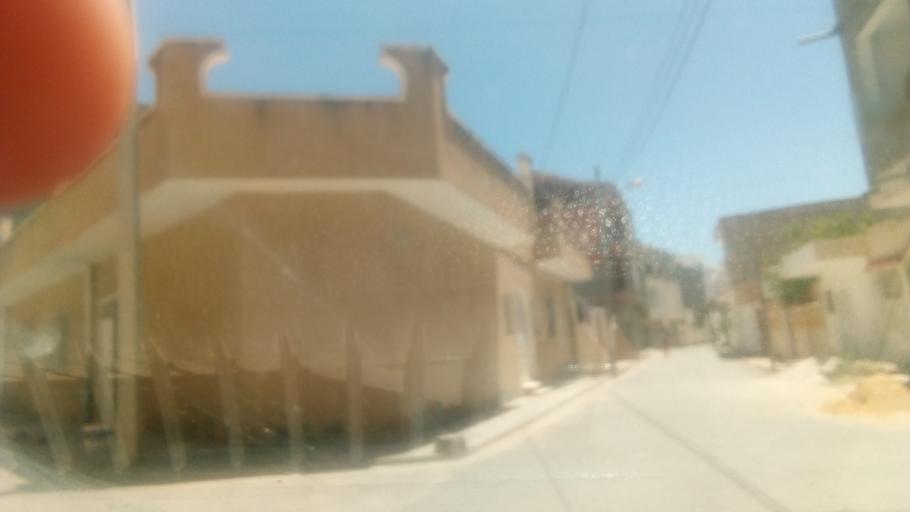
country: TN
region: Al Qayrawan
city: Kairouan
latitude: 35.6673
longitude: 10.0860
